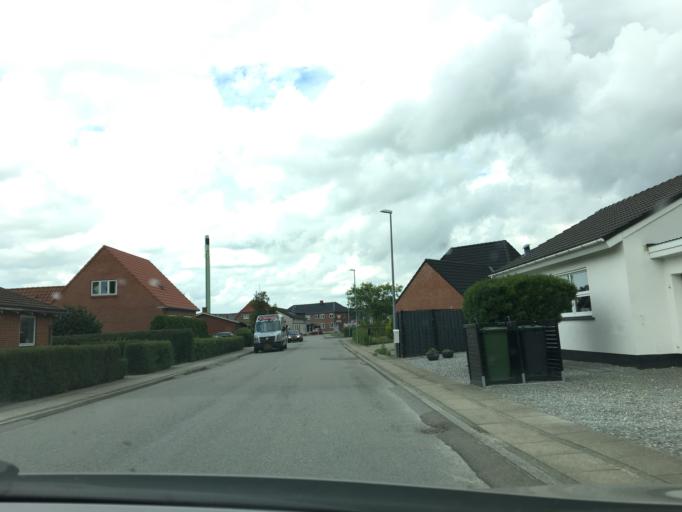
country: DK
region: South Denmark
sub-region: Varde Kommune
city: Oksbol
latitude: 55.7186
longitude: 8.3428
